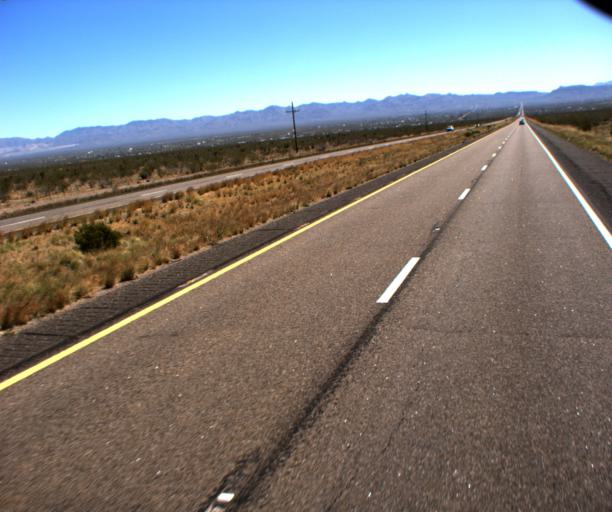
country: US
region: Arizona
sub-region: Mohave County
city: Golden Valley
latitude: 35.2274
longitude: -114.3294
